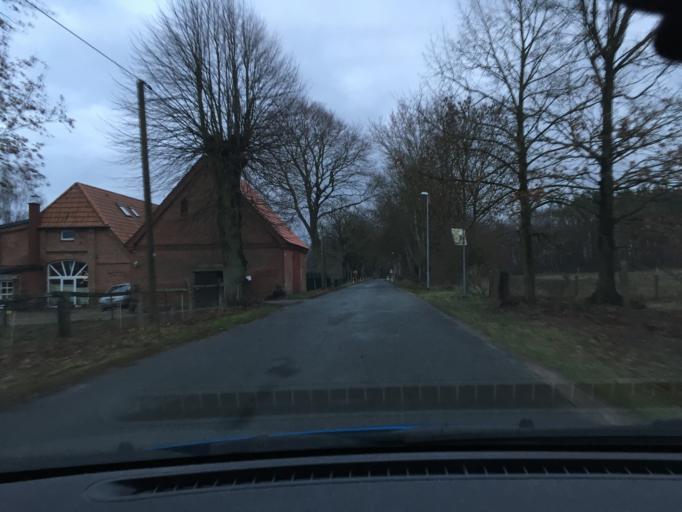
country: DE
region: Mecklenburg-Vorpommern
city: Boizenburg
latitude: 53.3873
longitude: 10.6903
